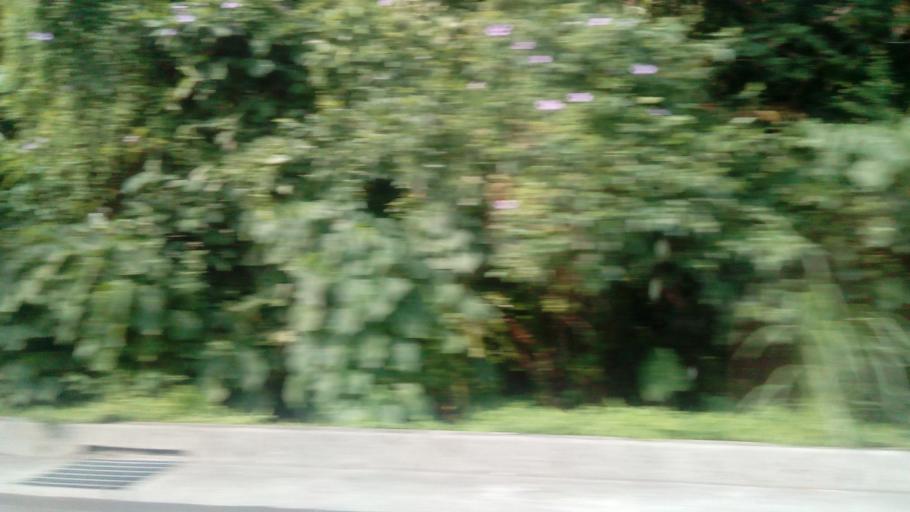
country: TW
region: Taiwan
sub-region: Yilan
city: Yilan
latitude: 24.5867
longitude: 121.8636
